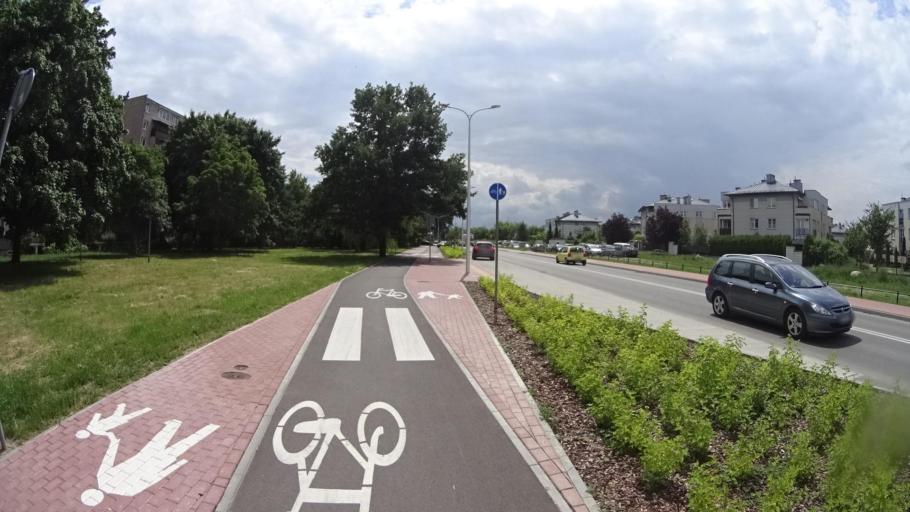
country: PL
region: Masovian Voivodeship
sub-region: Powiat pruszkowski
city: Granica
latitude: 52.1576
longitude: 20.7846
